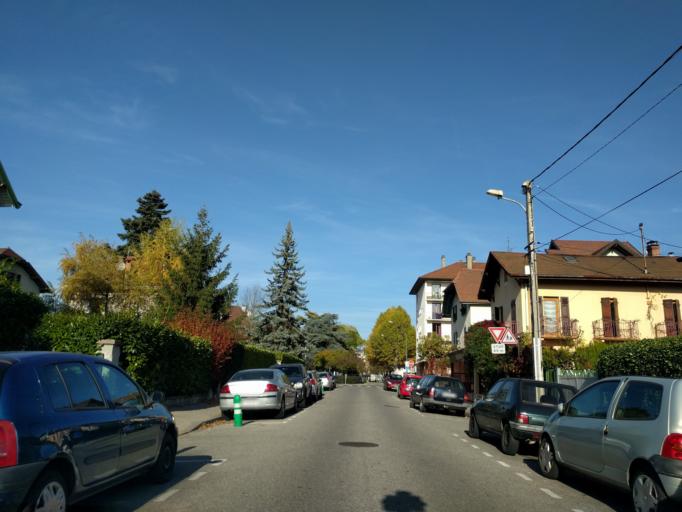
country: FR
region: Rhone-Alpes
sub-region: Departement de la Haute-Savoie
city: Annecy
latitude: 45.9079
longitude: 6.1189
